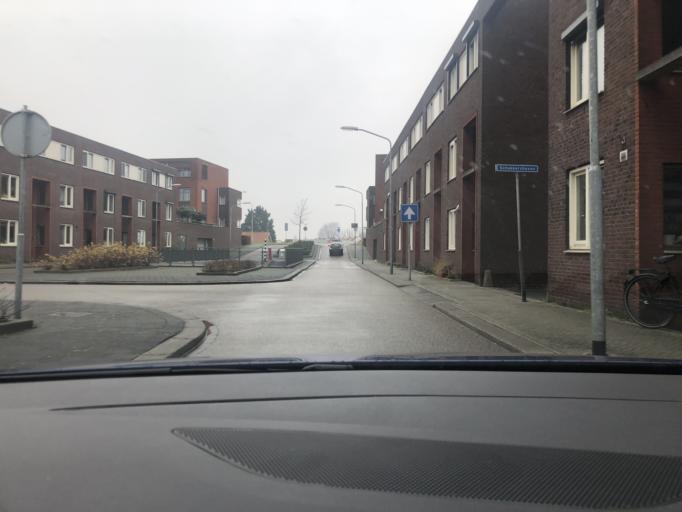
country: NL
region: South Holland
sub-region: Gemeente Zwijndrecht
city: Zwijndrecht
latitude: 51.8141
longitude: 4.6509
